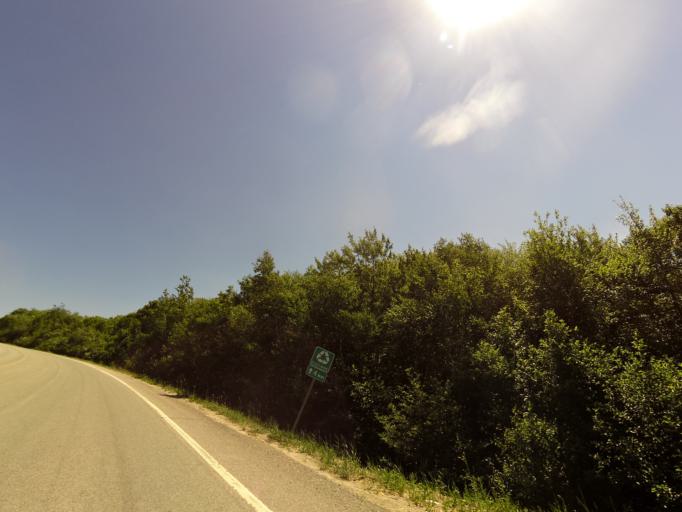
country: CA
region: Quebec
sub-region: Abitibi-Temiscamingue
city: Temiscaming
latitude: 46.7161
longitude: -79.0931
